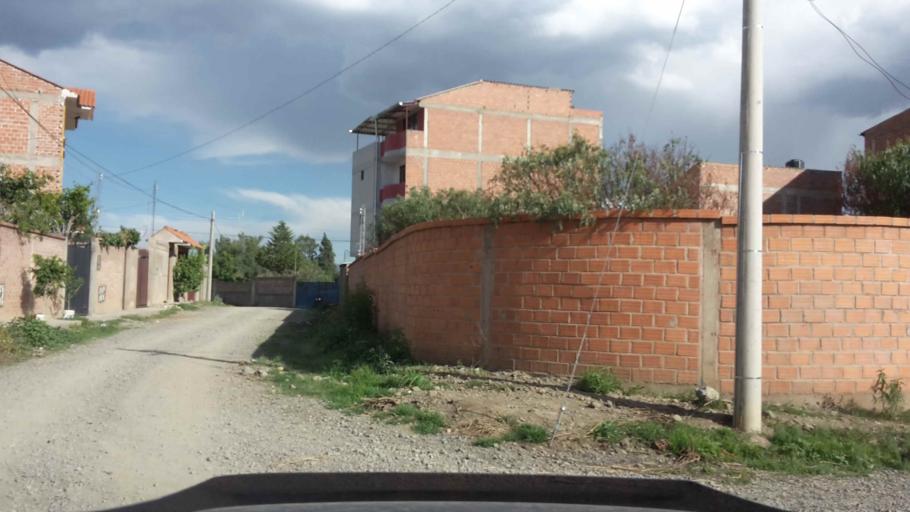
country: BO
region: Cochabamba
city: Cochabamba
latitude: -17.3344
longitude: -66.2155
